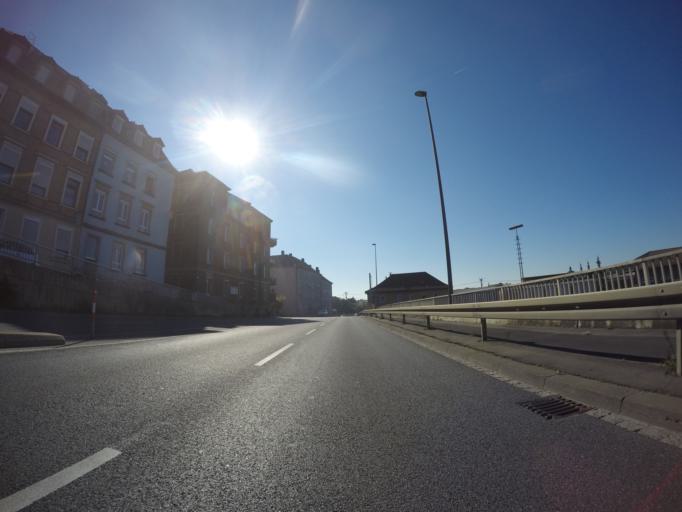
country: DE
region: Bavaria
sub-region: Regierungsbezirk Unterfranken
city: Wuerzburg
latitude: 49.8036
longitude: 9.9403
